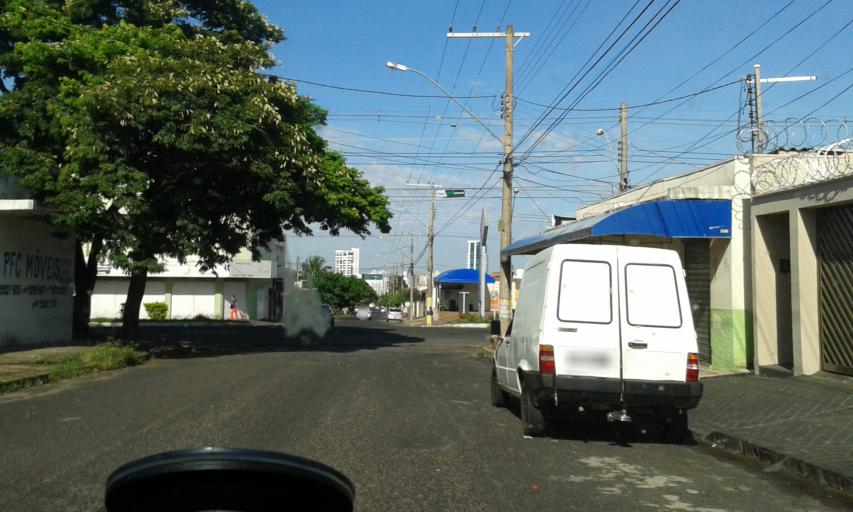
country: BR
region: Minas Gerais
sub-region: Uberlandia
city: Uberlandia
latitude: -18.9022
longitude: -48.2499
